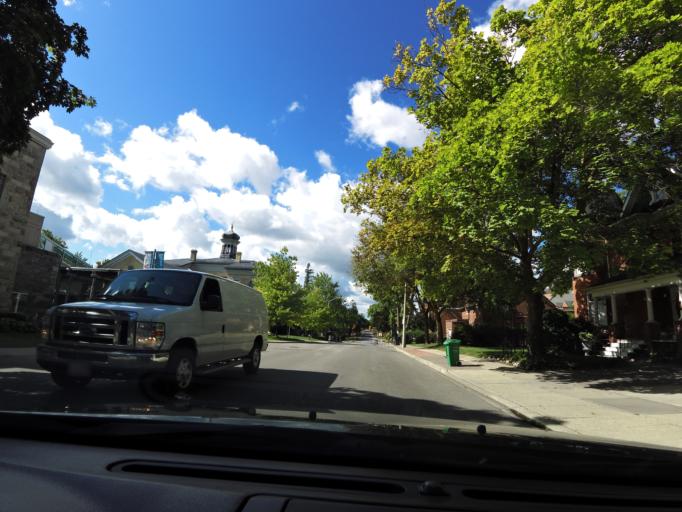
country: CA
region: Ontario
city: Brampton
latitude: 43.6856
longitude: -79.7573
